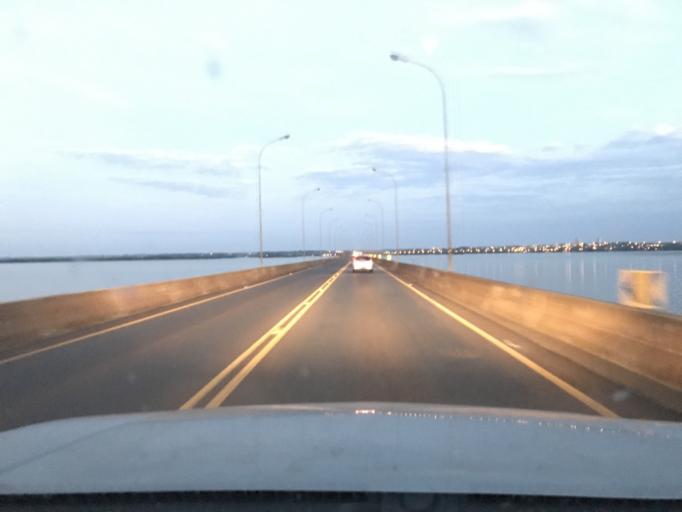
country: PY
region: Canindeyu
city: Salto del Guaira
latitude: -24.0459
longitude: -54.2708
